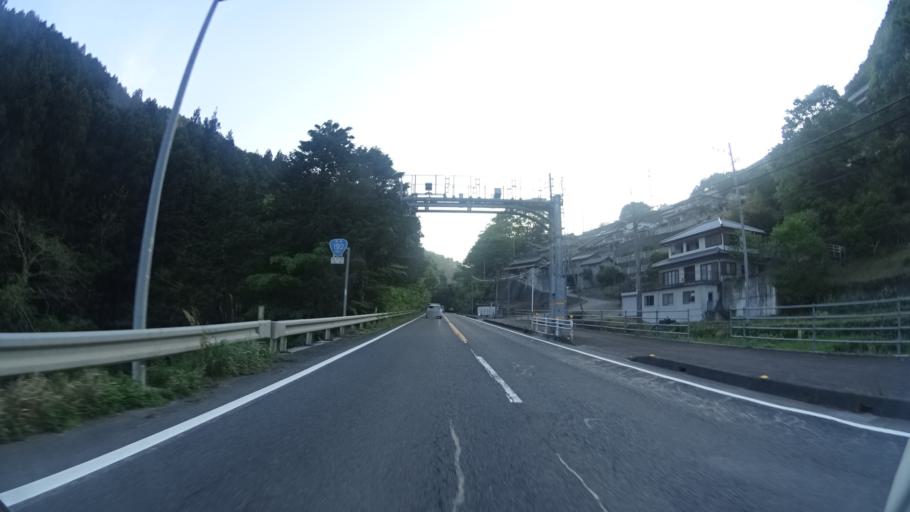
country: JP
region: Tokushima
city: Ikedacho
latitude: 34.0079
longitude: 133.7243
